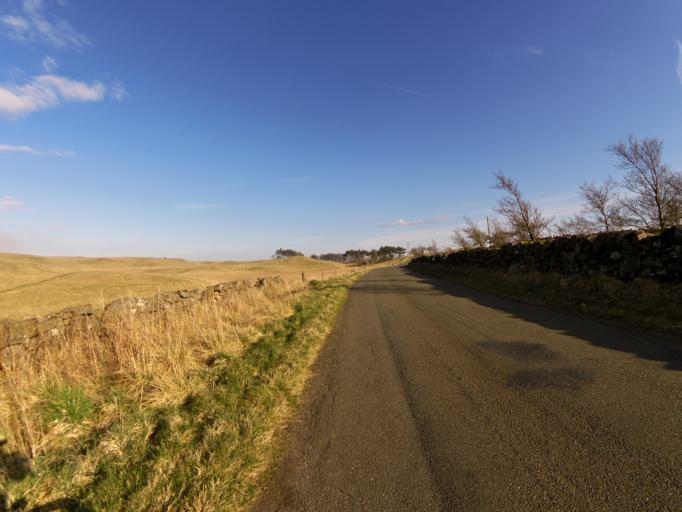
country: GB
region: Scotland
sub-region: Fife
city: Falkland
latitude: 56.2383
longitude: -3.2465
